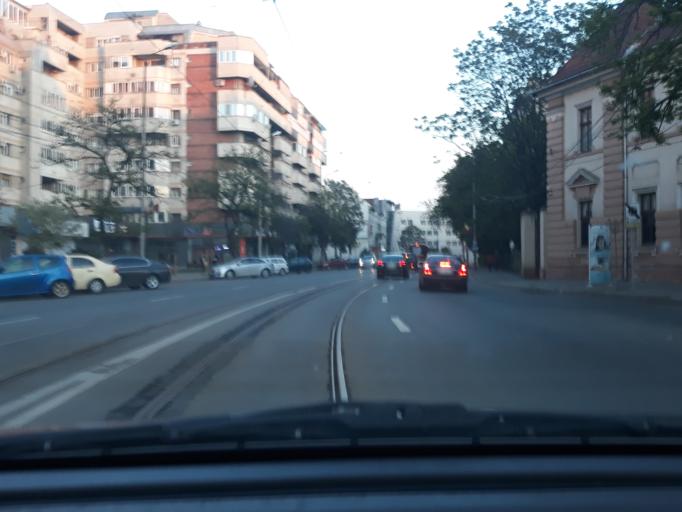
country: RO
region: Bihor
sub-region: Comuna Biharea
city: Oradea
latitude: 47.0610
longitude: 21.9391
